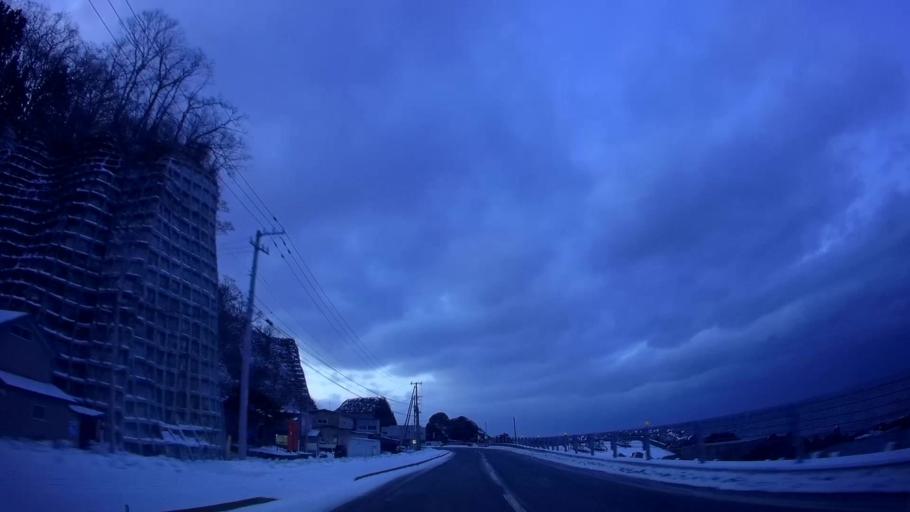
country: JP
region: Hokkaido
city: Hakodate
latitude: 41.8902
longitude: 141.0554
